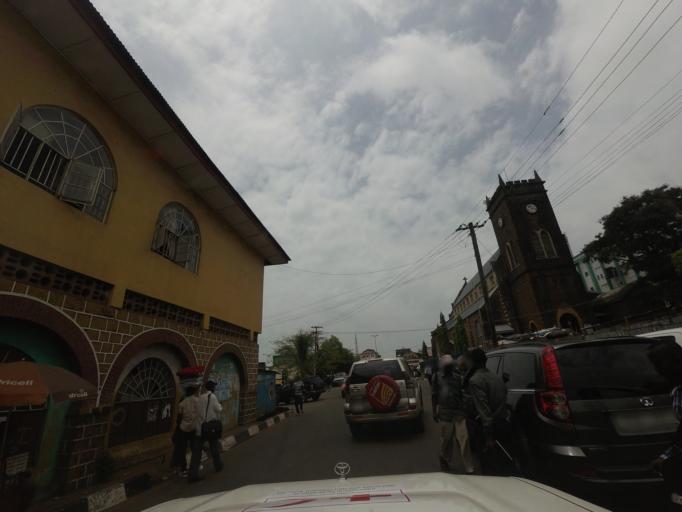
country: SL
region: Western Area
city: Freetown
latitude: 8.4898
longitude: -13.2364
